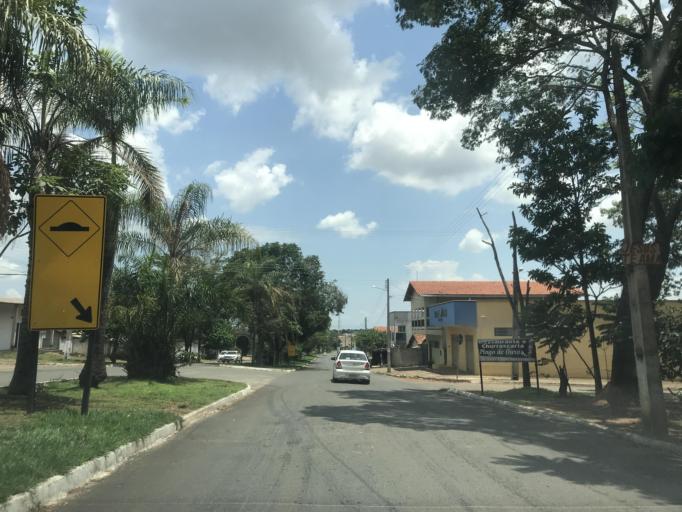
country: BR
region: Goias
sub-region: Bela Vista De Goias
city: Bela Vista de Goias
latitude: -17.0545
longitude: -48.6658
